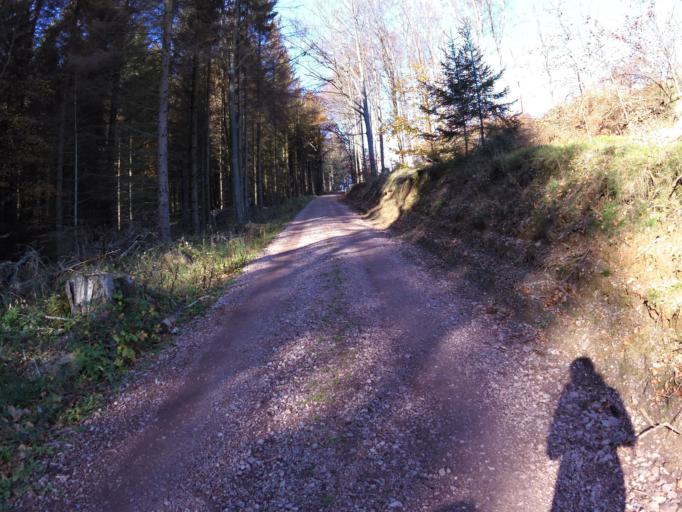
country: DE
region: Thuringia
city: Ruhla
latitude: 50.9029
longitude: 10.3447
